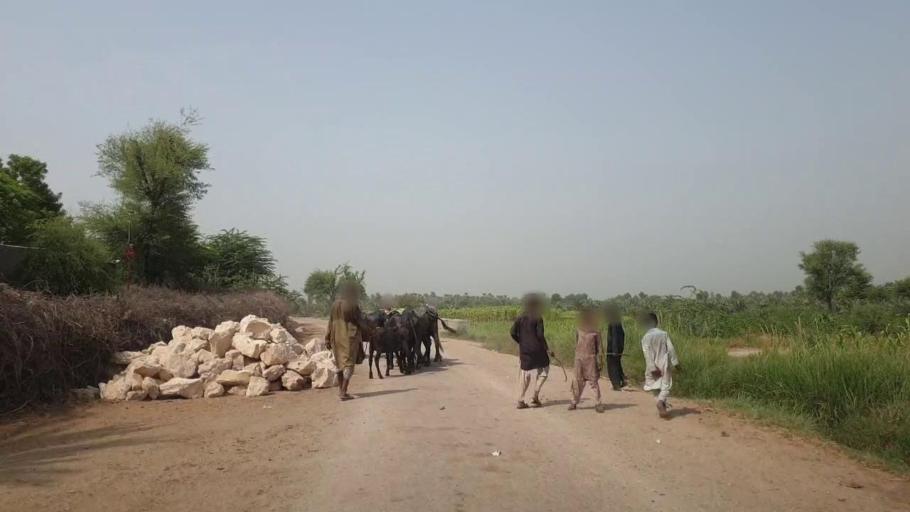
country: PK
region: Sindh
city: Gambat
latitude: 27.4035
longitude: 68.5539
